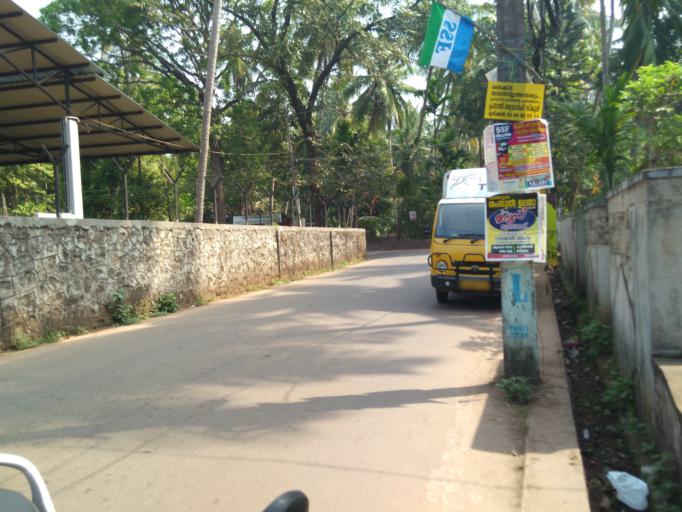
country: IN
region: Kerala
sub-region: Kozhikode
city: Kunnamangalam
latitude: 11.2921
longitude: 75.8364
